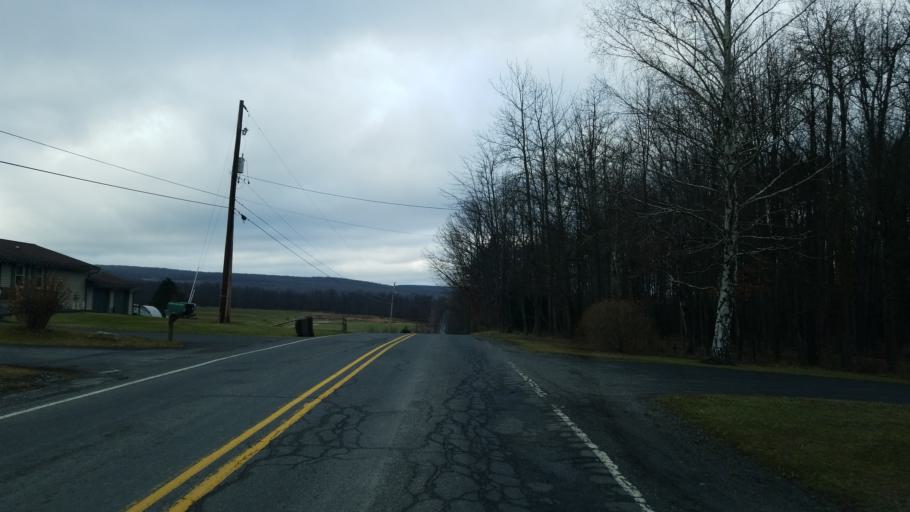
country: US
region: Pennsylvania
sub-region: Clearfield County
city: Hyde
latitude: 41.0407
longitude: -78.4892
